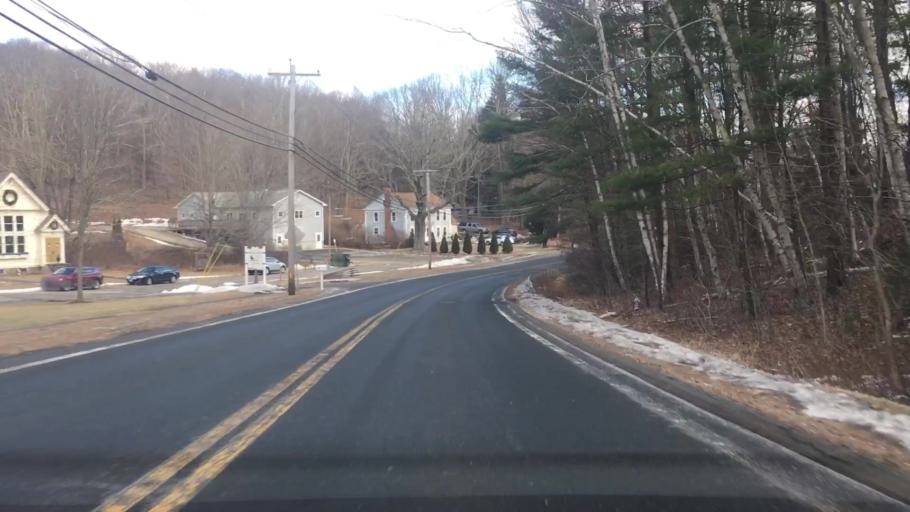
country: US
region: Massachusetts
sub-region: Hampden County
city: Wales
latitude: 42.0742
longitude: -72.2160
